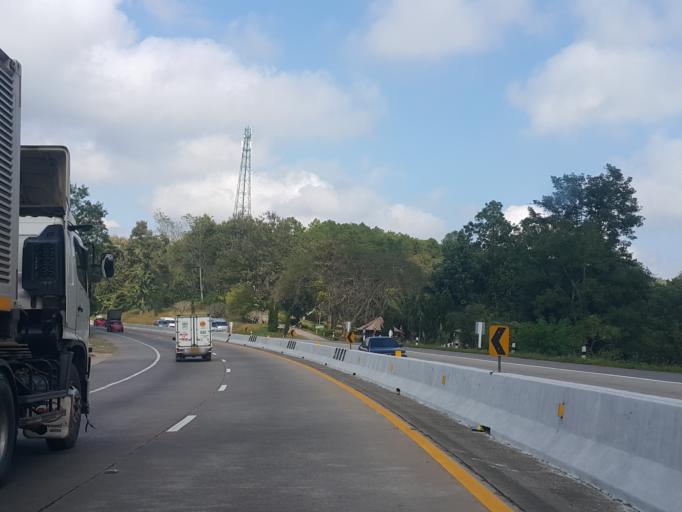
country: TH
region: Lampang
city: Hang Chat
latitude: 18.3338
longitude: 99.2506
